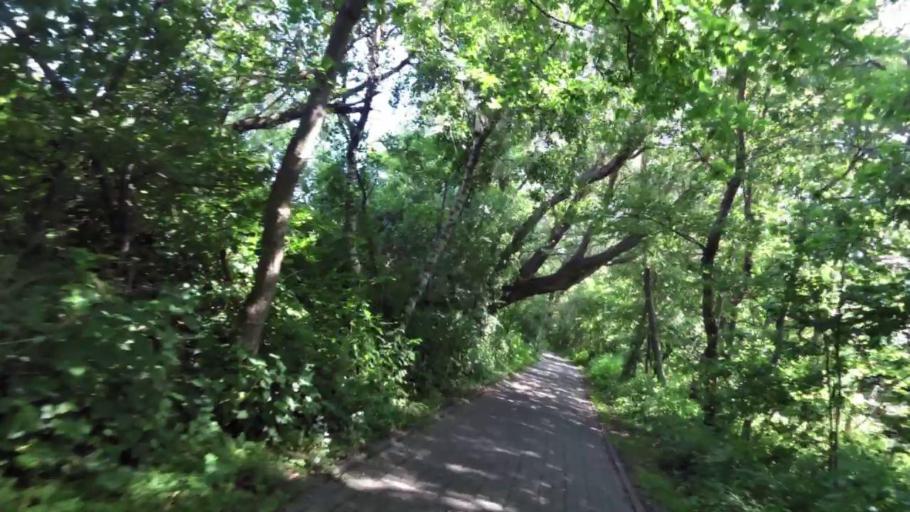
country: PL
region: West Pomeranian Voivodeship
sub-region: Powiat kolobrzeski
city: Kolobrzeg
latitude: 54.1951
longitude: 15.6357
